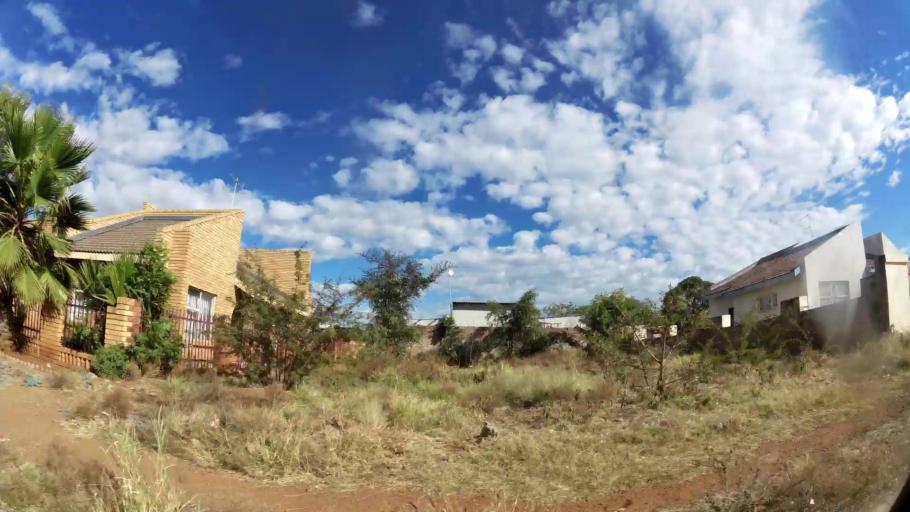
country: ZA
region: Limpopo
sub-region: Waterberg District Municipality
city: Warmbaths
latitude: -24.8788
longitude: 28.2731
